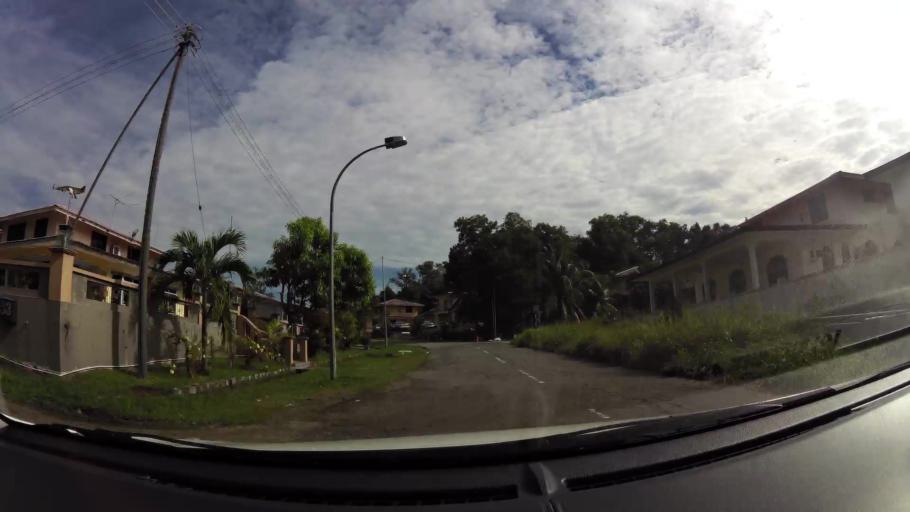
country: BN
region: Brunei and Muara
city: Bandar Seri Begawan
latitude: 4.9217
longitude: 114.8970
